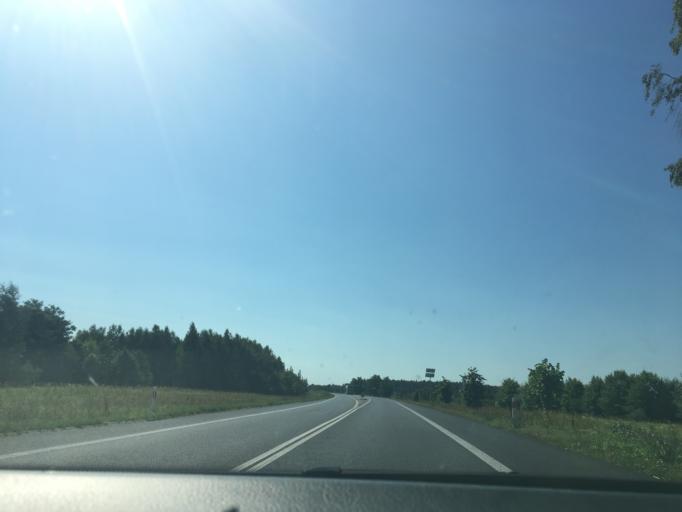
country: PL
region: Lublin Voivodeship
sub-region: Powiat lubartowski
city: Lubartow
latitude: 51.4539
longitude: 22.5770
